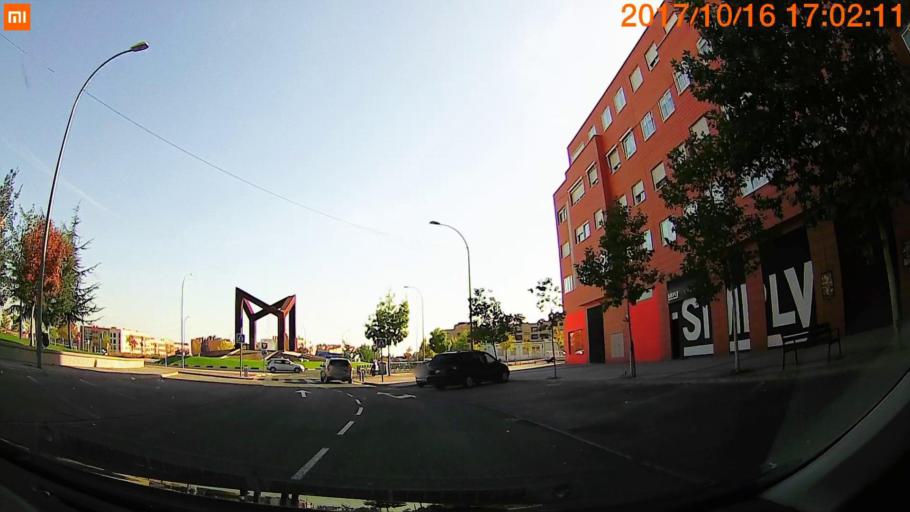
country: ES
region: Madrid
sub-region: Provincia de Madrid
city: Alcobendas
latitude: 40.5557
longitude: -3.6599
